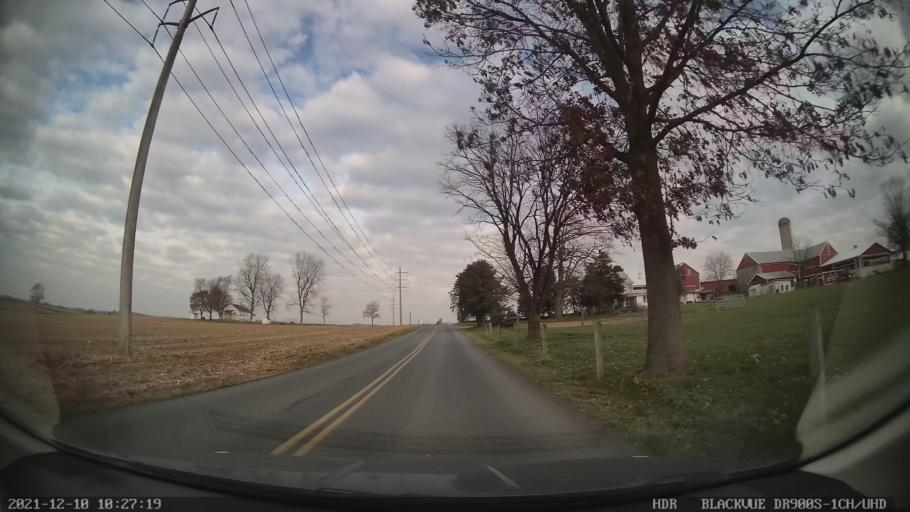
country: US
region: Pennsylvania
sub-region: Berks County
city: Kutztown
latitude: 40.5067
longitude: -75.7457
